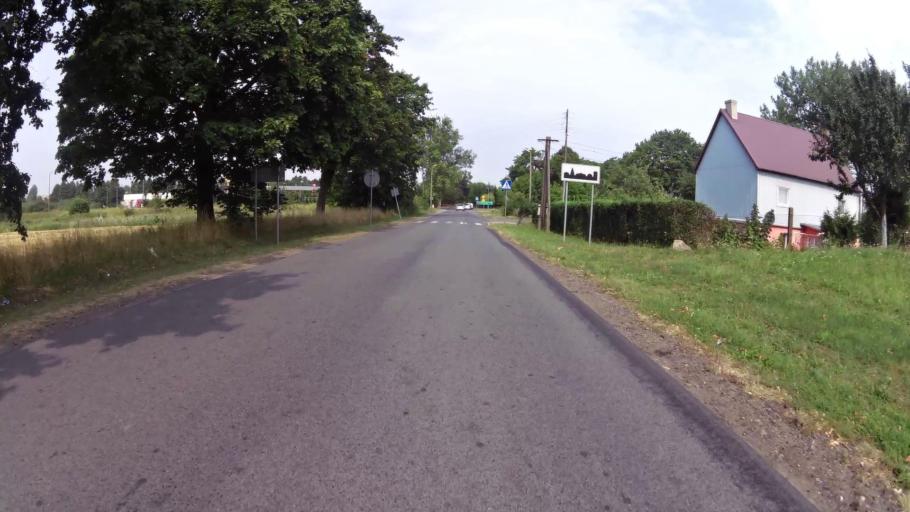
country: PL
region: West Pomeranian Voivodeship
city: Trzcinsko Zdroj
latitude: 52.9609
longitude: 14.6179
